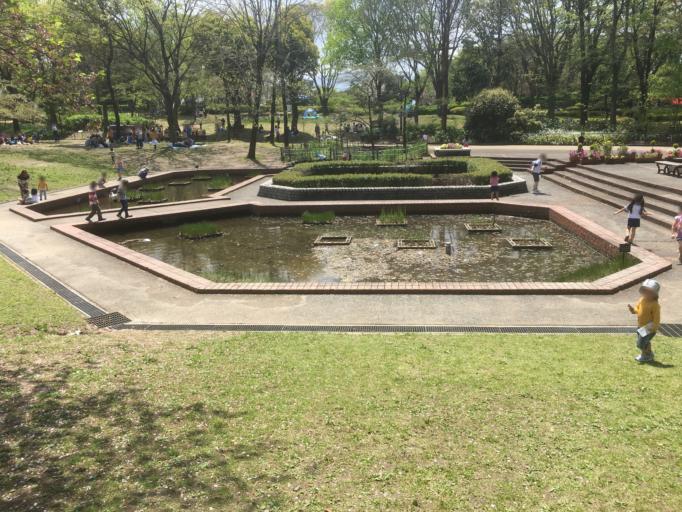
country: JP
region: Fukuoka
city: Fukuoka-shi
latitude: 33.5711
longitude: 130.3914
